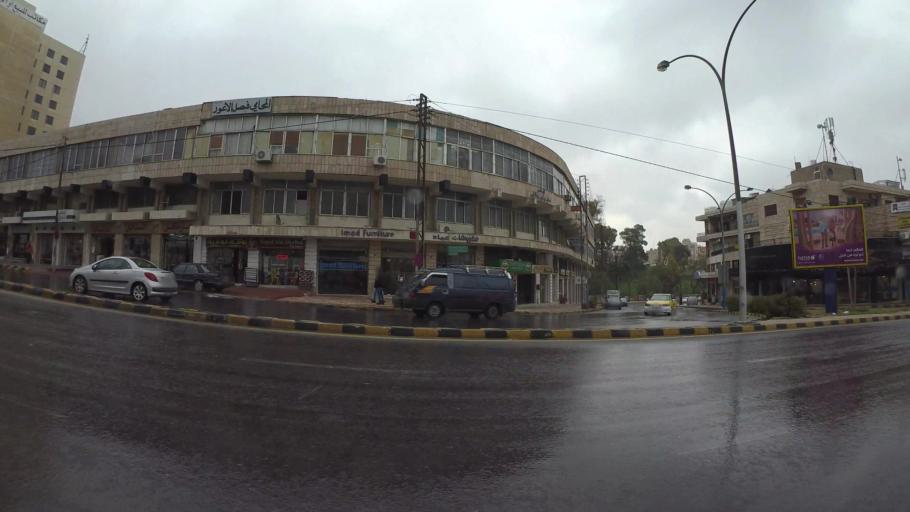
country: JO
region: Amman
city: Amman
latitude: 31.9655
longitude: 35.9108
